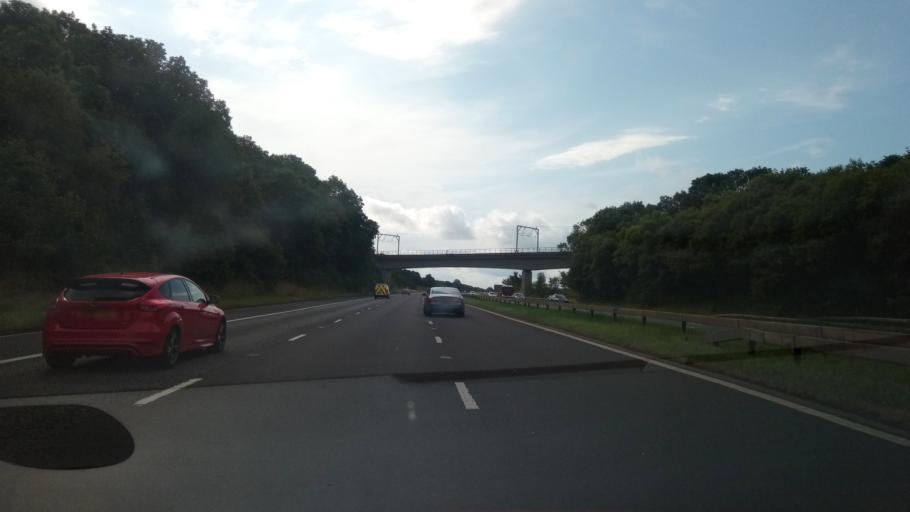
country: GB
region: England
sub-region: Cumbria
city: Penrith
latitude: 54.6364
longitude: -2.7294
